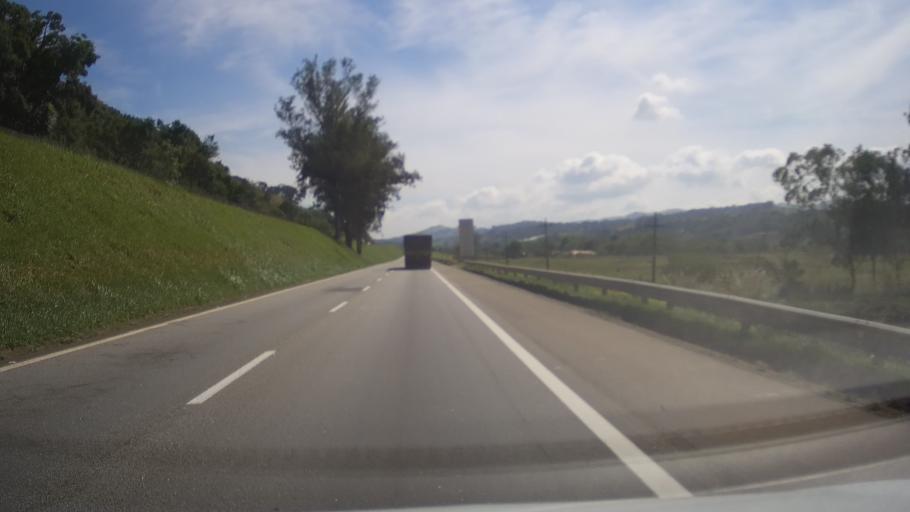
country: BR
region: Minas Gerais
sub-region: Cambui
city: Cambui
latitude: -22.5871
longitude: -46.0501
